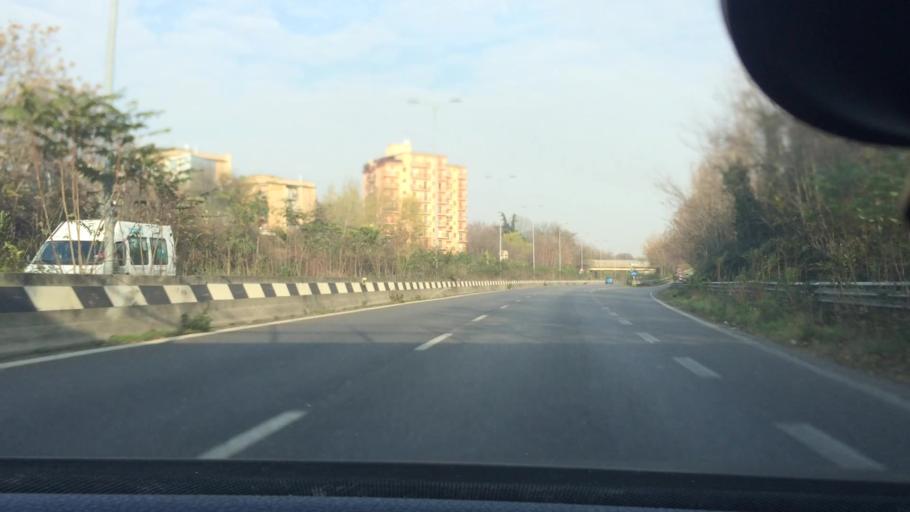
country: IT
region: Lombardy
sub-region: Citta metropolitana di Milano
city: Cormano
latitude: 45.5443
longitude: 9.1619
